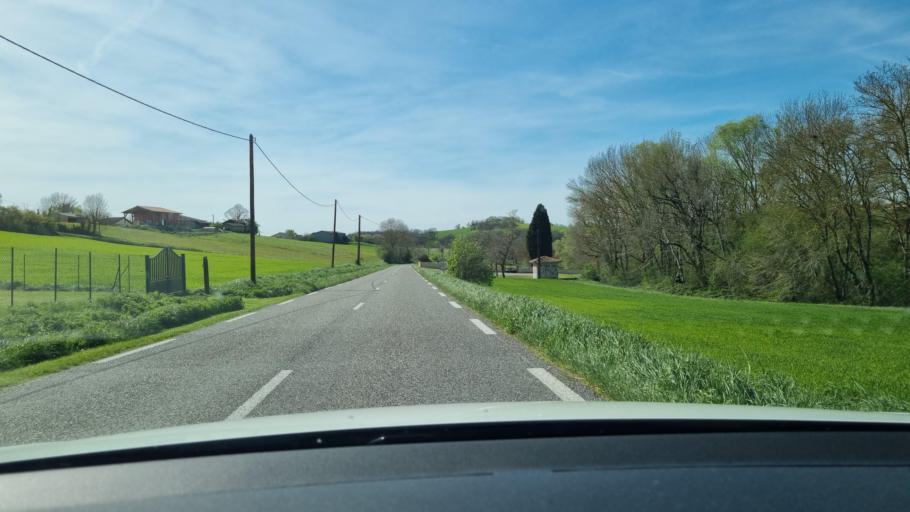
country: FR
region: Midi-Pyrenees
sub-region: Departement du Gers
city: Samatan
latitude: 43.4908
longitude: 1.0075
